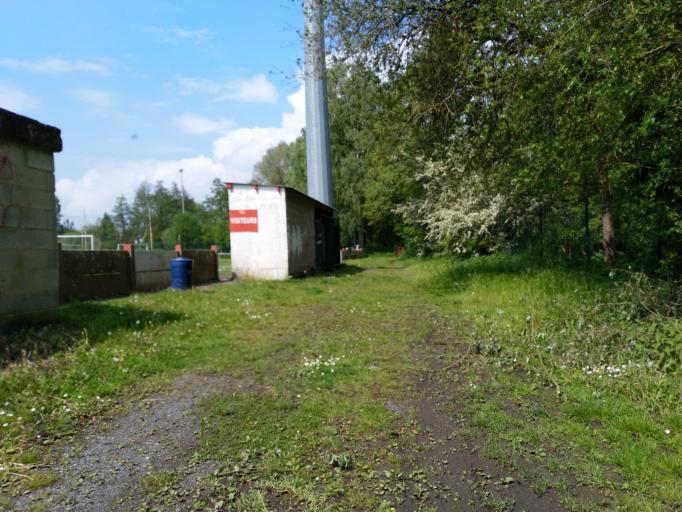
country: BE
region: Wallonia
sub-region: Province du Hainaut
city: Chasse Royale
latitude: 50.4385
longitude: 3.9661
